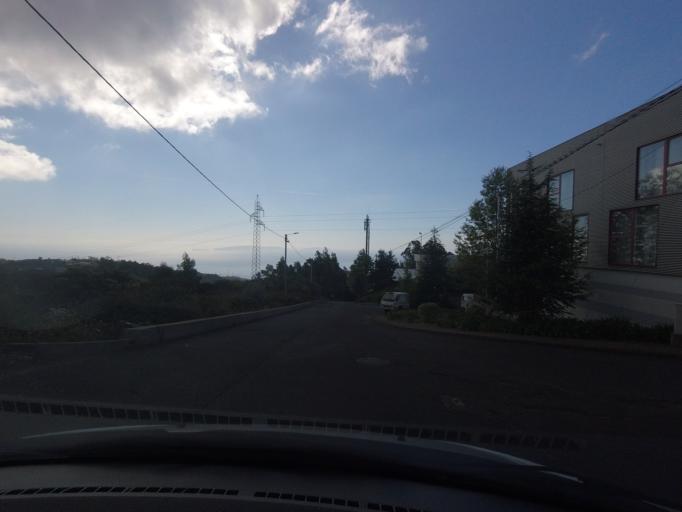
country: PT
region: Madeira
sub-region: Santa Cruz
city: Camacha
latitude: 32.6680
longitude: -16.8547
